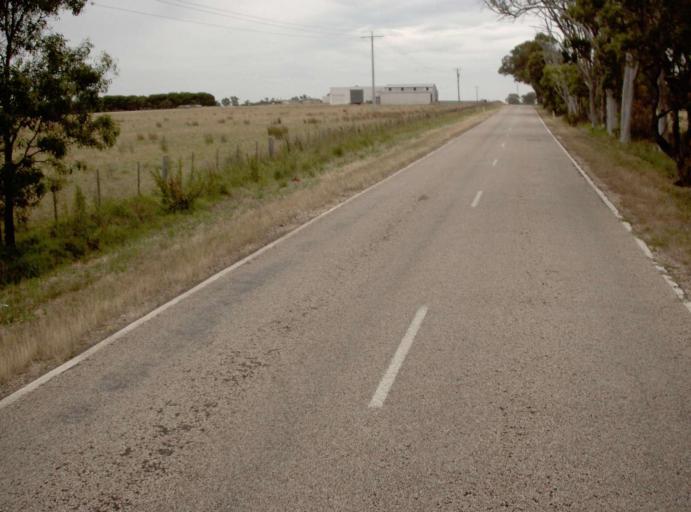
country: AU
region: Victoria
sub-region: East Gippsland
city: Bairnsdale
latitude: -37.8535
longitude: 147.4285
